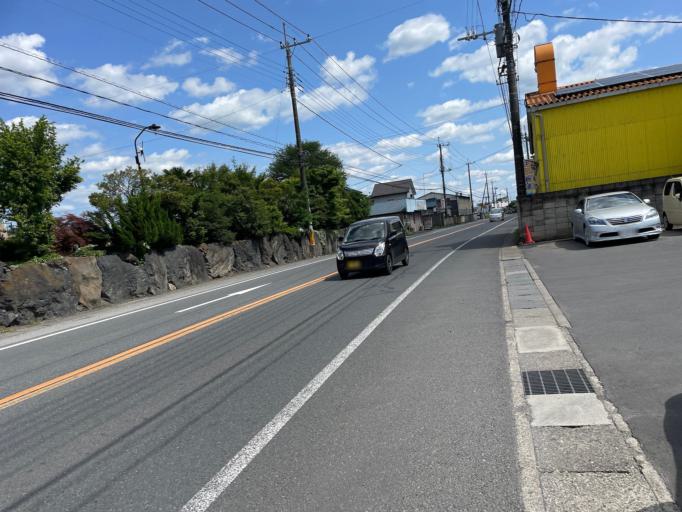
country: JP
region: Tochigi
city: Sano
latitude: 36.3225
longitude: 139.6405
